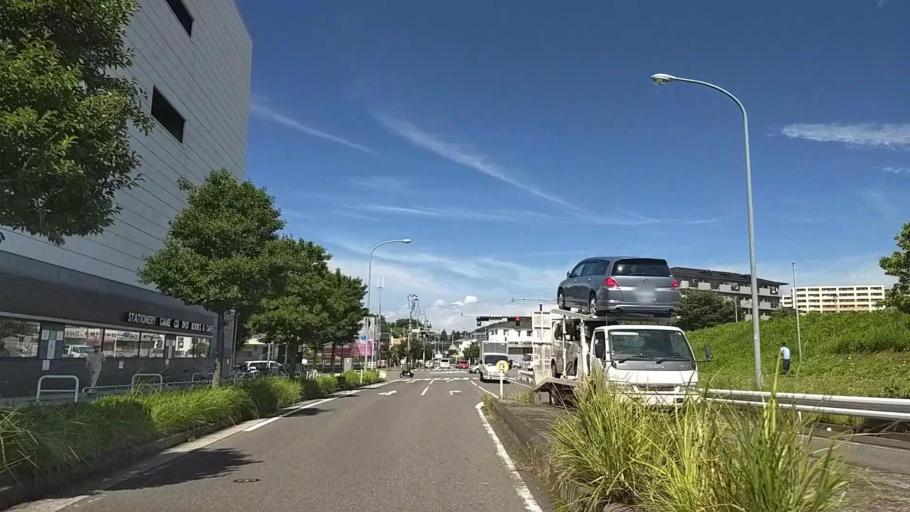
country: JP
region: Tokyo
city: Chofugaoka
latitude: 35.5510
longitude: 139.5759
